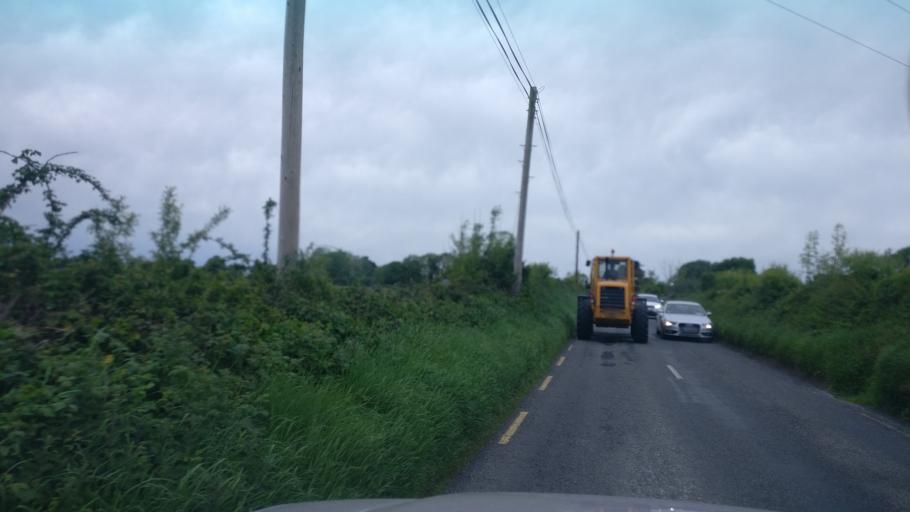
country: IE
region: Connaught
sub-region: County Galway
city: Portumna
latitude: 53.0937
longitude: -8.2379
